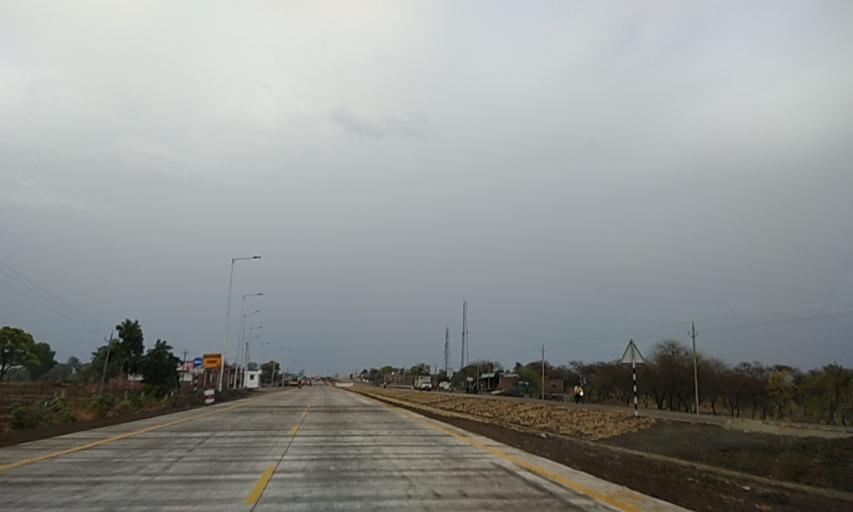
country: IN
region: Madhya Pradesh
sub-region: Rajgarh
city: Sarangpur
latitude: 23.6228
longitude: 76.5609
